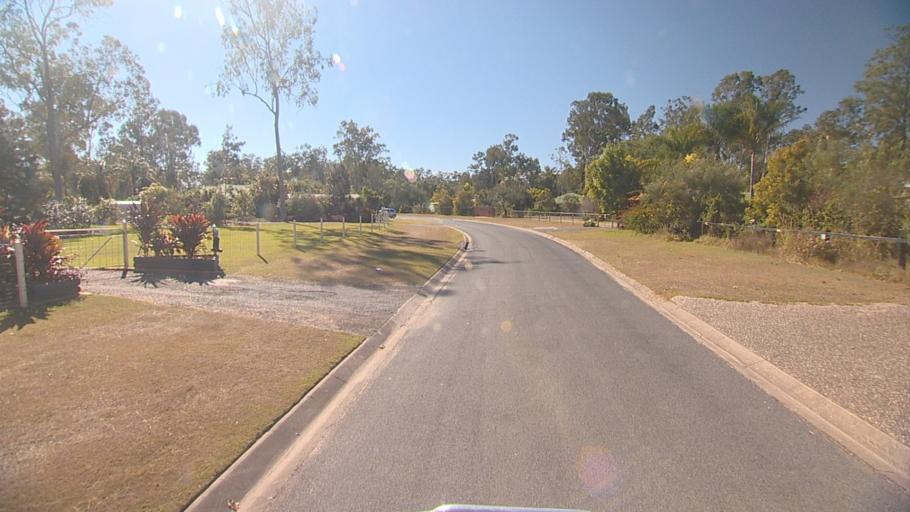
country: AU
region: Queensland
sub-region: Logan
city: North Maclean
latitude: -27.8166
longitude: 152.9502
